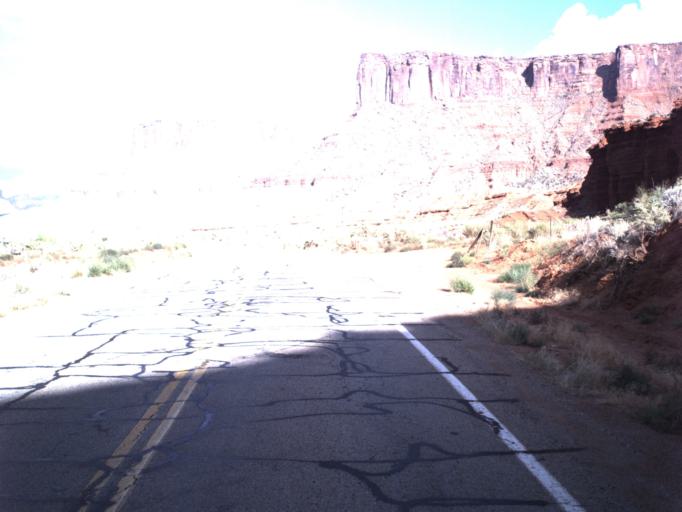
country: US
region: Utah
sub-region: Grand County
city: Moab
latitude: 38.6815
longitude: -109.4346
